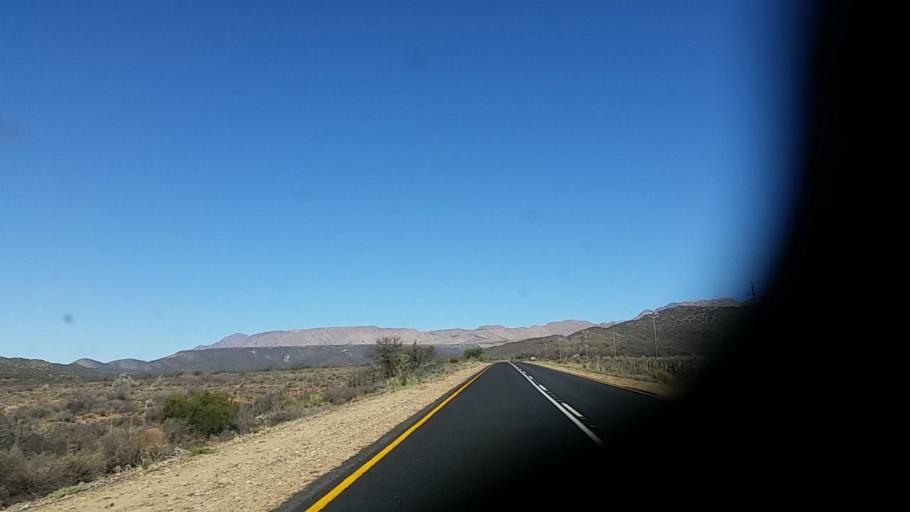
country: ZA
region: Western Cape
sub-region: Eden District Municipality
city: George
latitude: -33.5388
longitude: 22.7227
